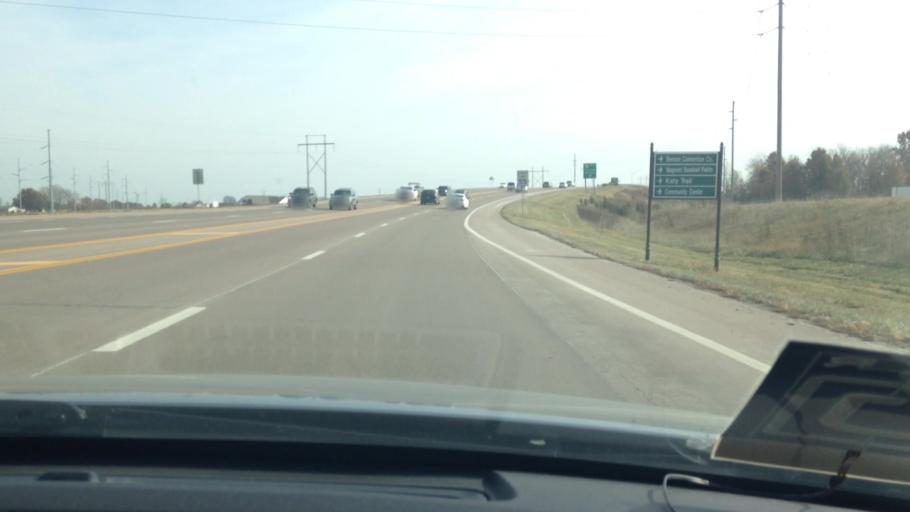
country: US
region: Missouri
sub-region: Henry County
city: Clinton
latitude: 38.3878
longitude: -93.7597
